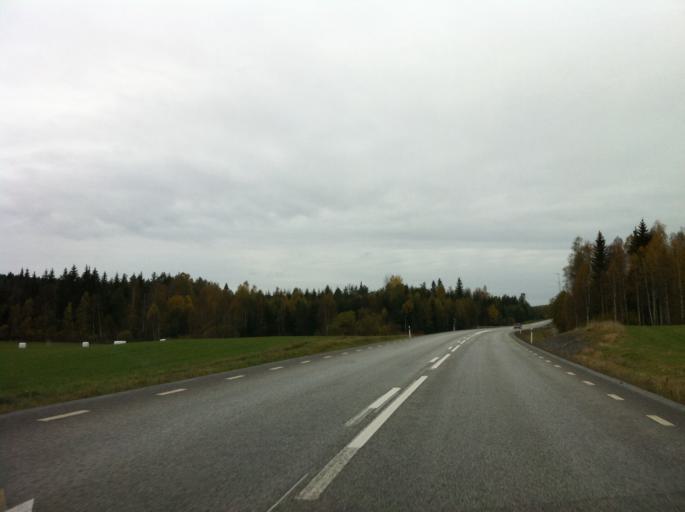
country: SE
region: OErebro
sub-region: Ljusnarsbergs Kommun
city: Kopparberg
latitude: 59.8455
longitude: 15.0726
